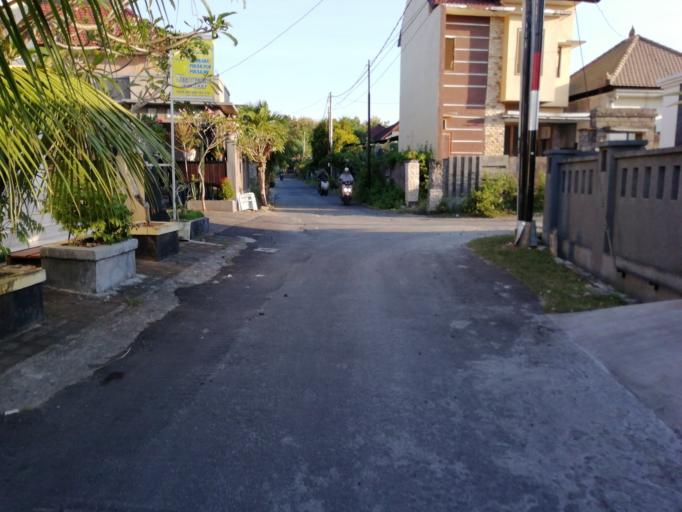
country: ID
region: Bali
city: Bualu
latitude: -8.8007
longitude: 115.1961
